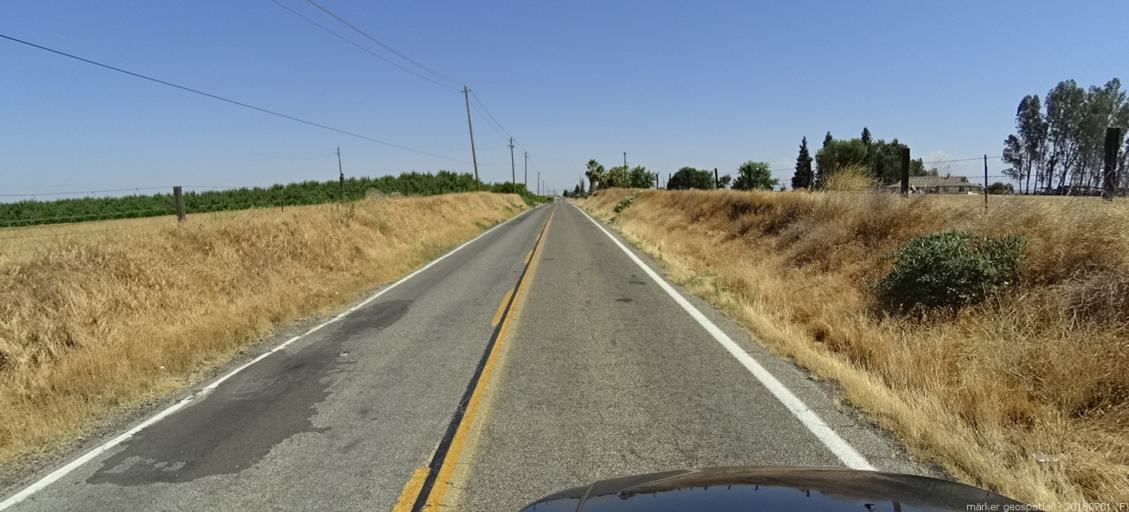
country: US
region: California
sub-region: Madera County
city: Madera Acres
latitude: 37.0268
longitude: -120.0290
